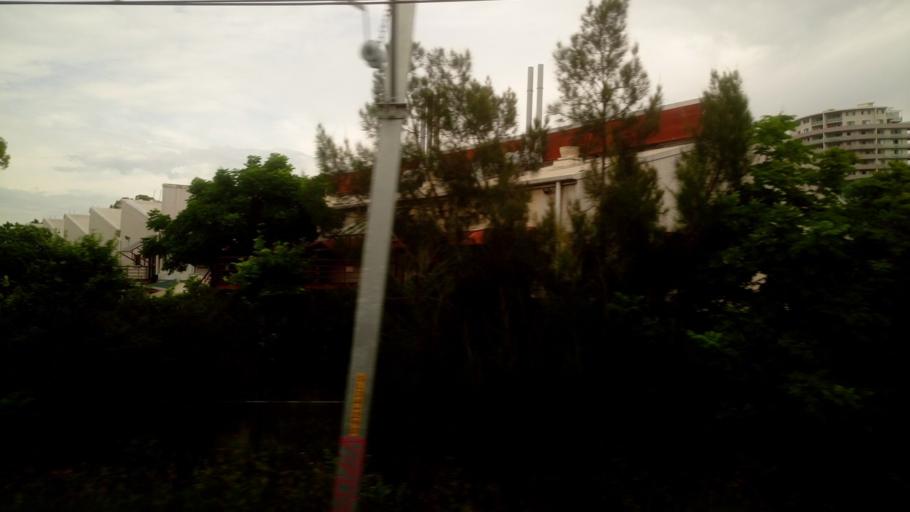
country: AU
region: New South Wales
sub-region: Blacktown
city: Blacktown
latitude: -33.7709
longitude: 150.9136
